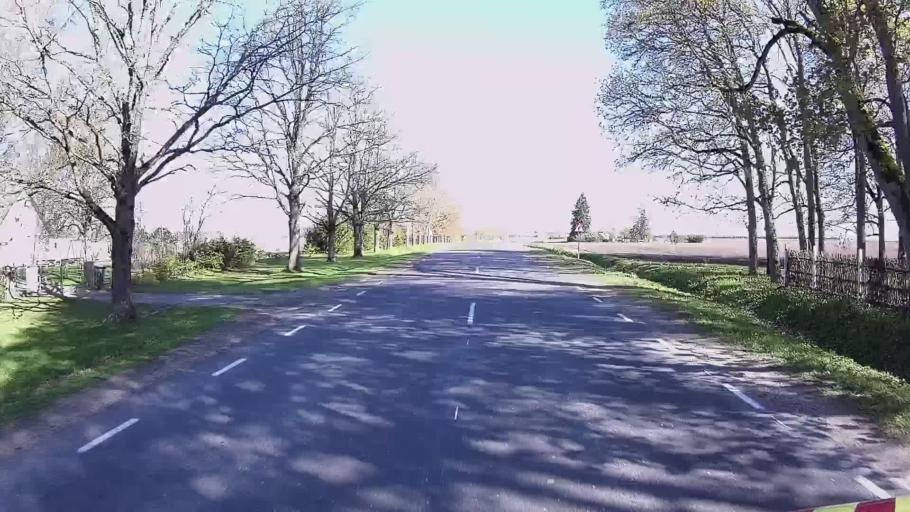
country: EE
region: Jaervamaa
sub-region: Paide linn
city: Paide
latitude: 58.8915
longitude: 25.7138
